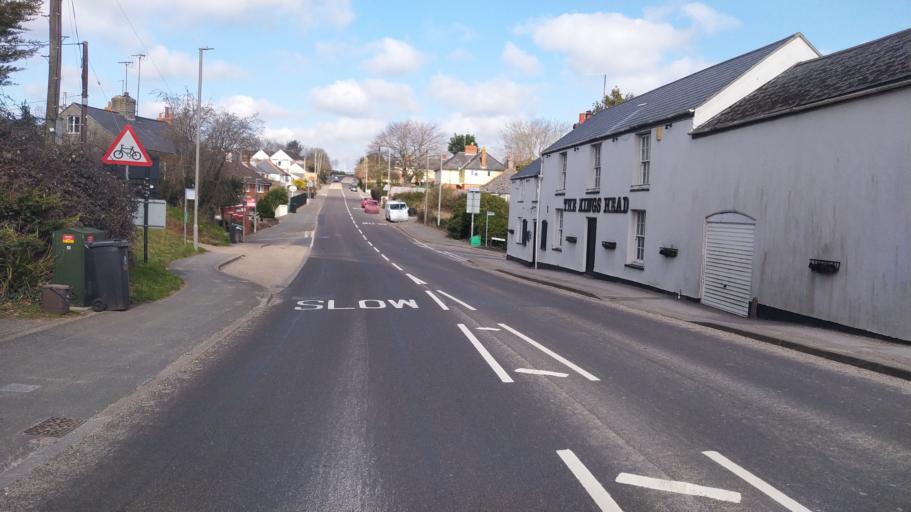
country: GB
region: England
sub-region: Dorset
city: Bridport
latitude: 50.7443
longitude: -2.7416
